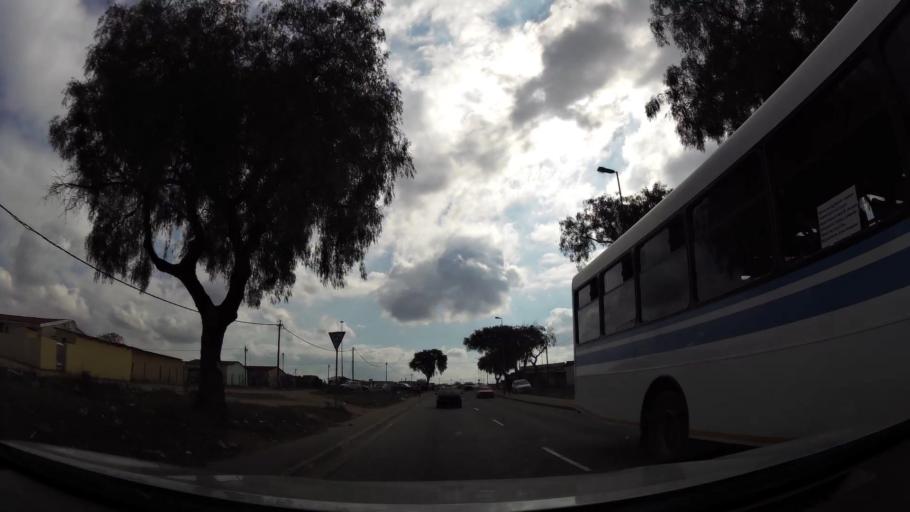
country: ZA
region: Eastern Cape
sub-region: Nelson Mandela Bay Metropolitan Municipality
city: Port Elizabeth
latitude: -33.8029
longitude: 25.5876
